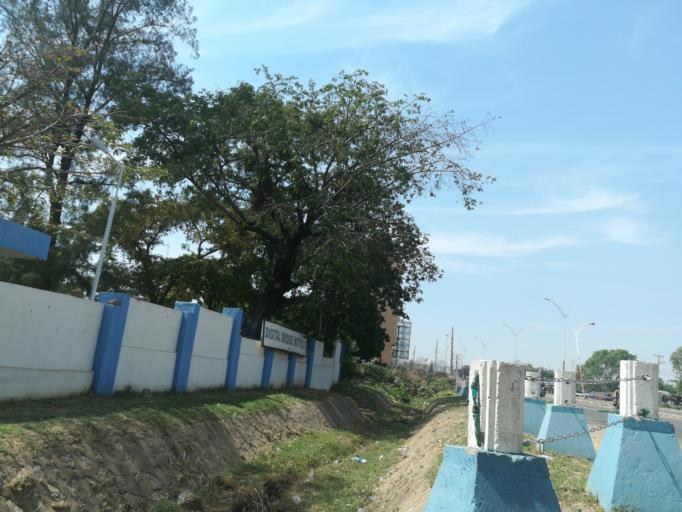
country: NG
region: Kano
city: Kano
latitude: 12.0285
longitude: 8.5181
